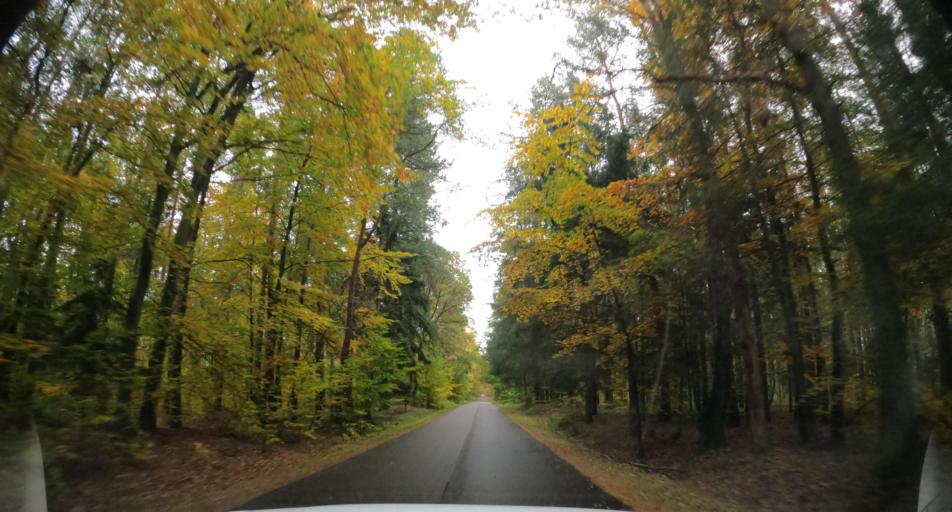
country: PL
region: West Pomeranian Voivodeship
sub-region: Powiat kamienski
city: Wolin
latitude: 53.9164
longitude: 14.5613
